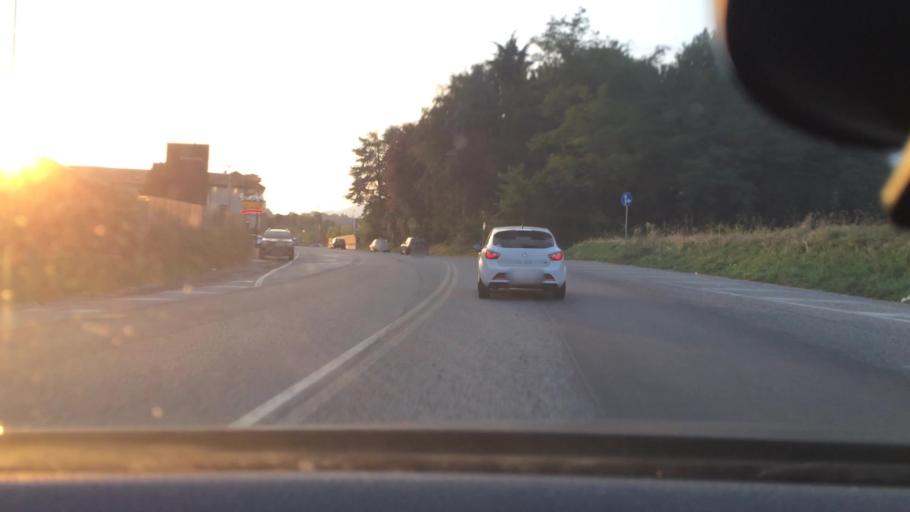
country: IT
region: Lombardy
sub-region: Provincia di Como
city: Anzano del Parco
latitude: 45.7606
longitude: 9.2076
